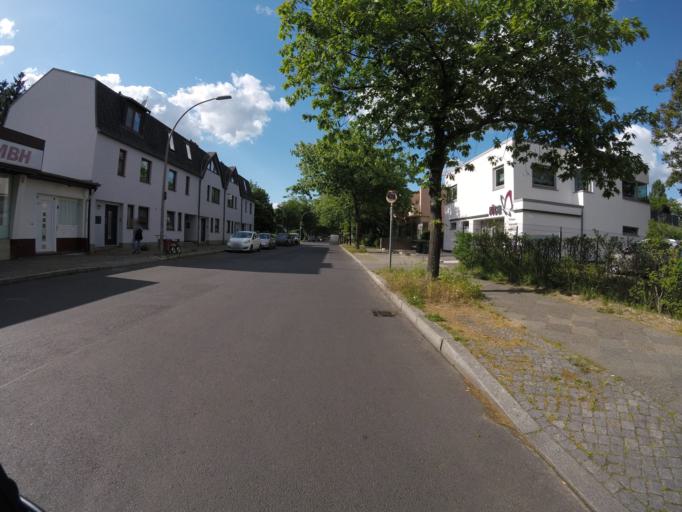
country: DE
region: Berlin
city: Wilhelmstadt
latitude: 52.5266
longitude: 13.1817
